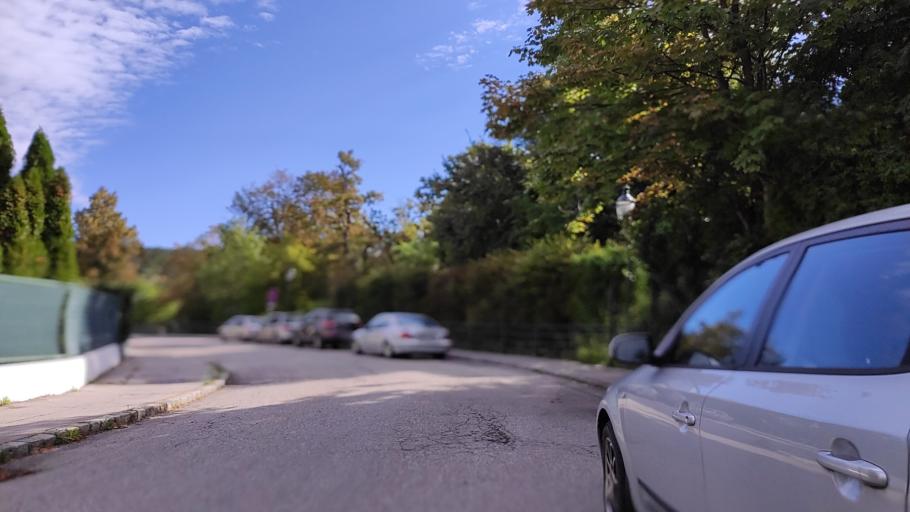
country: AT
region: Lower Austria
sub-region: Politischer Bezirk Baden
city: Baden
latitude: 48.0078
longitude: 16.2195
